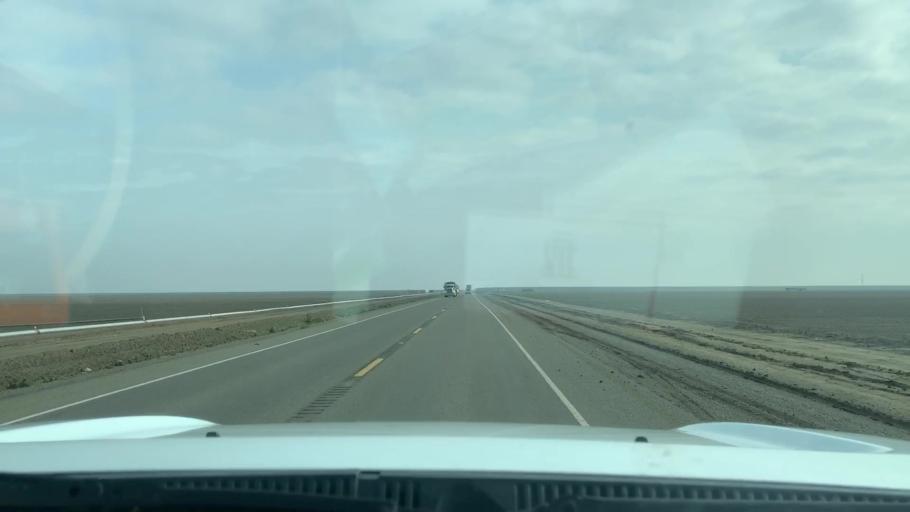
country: US
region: California
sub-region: Fresno County
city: Huron
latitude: 36.2554
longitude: -120.0274
